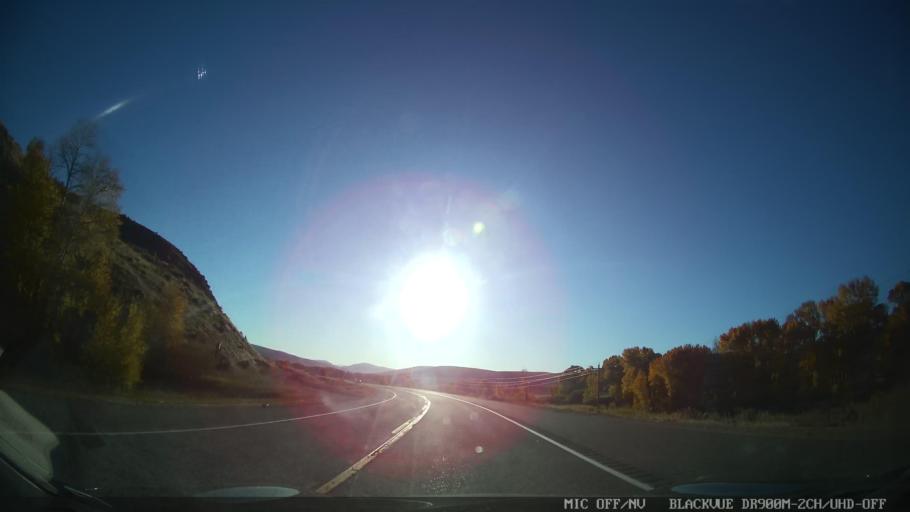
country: US
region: Colorado
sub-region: Grand County
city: Kremmling
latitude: 40.0629
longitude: -106.2509
